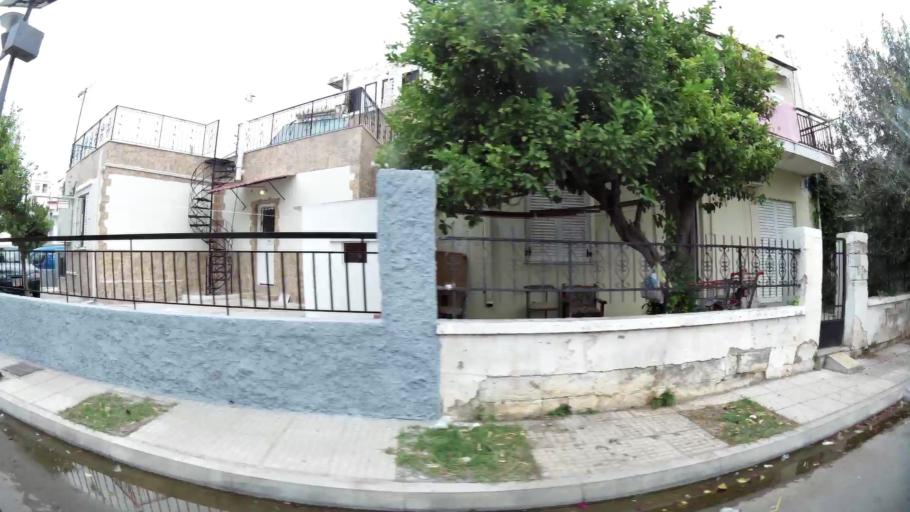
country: GR
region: Attica
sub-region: Nomarchia Athinas
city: Aigaleo
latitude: 37.9831
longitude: 23.6788
